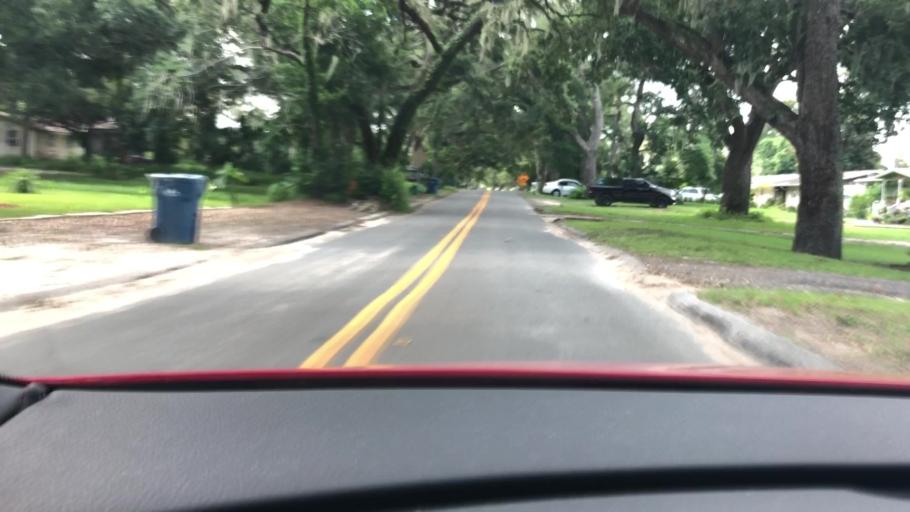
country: US
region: Florida
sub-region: Volusia County
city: Ormond Beach
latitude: 29.2673
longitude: -81.0519
